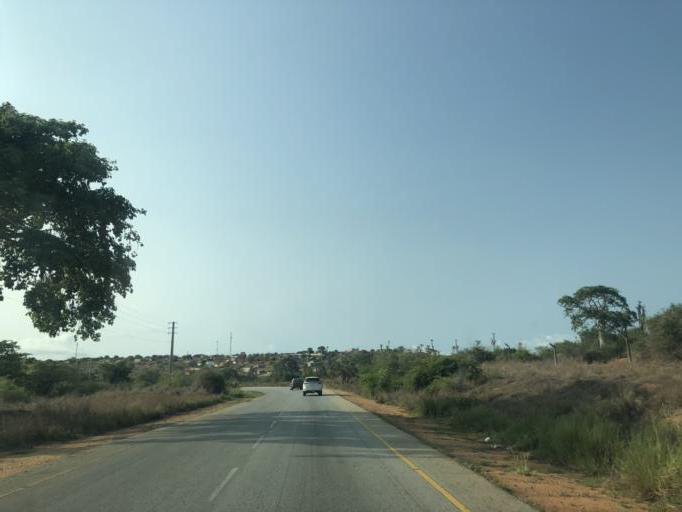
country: AO
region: Luanda
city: Luanda
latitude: -9.2972
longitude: 13.1344
